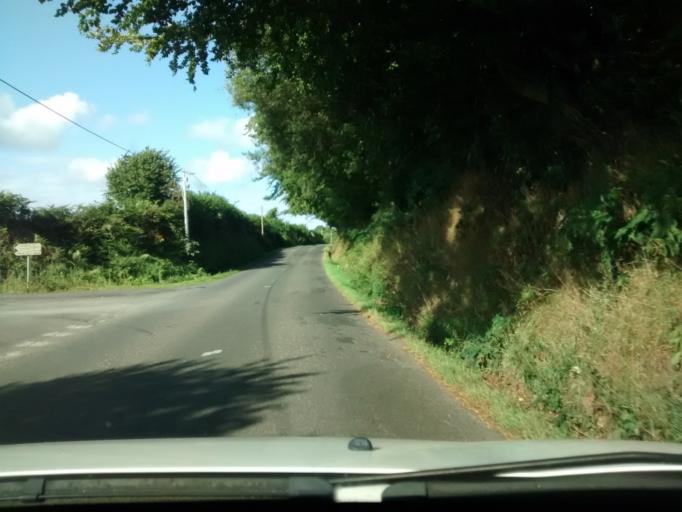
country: FR
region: Brittany
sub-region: Departement des Cotes-d'Armor
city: Rospez
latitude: 48.7537
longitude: -3.4083
